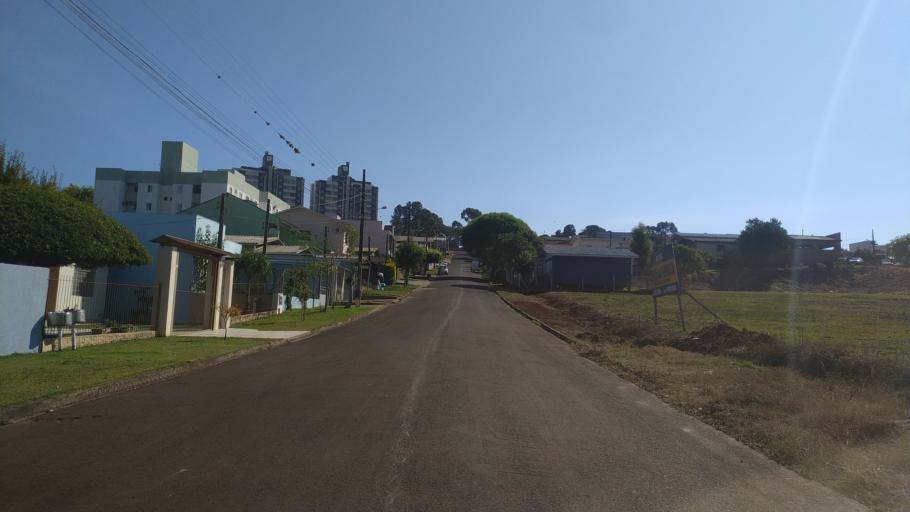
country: BR
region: Santa Catarina
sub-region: Chapeco
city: Chapeco
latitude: -27.0763
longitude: -52.6076
